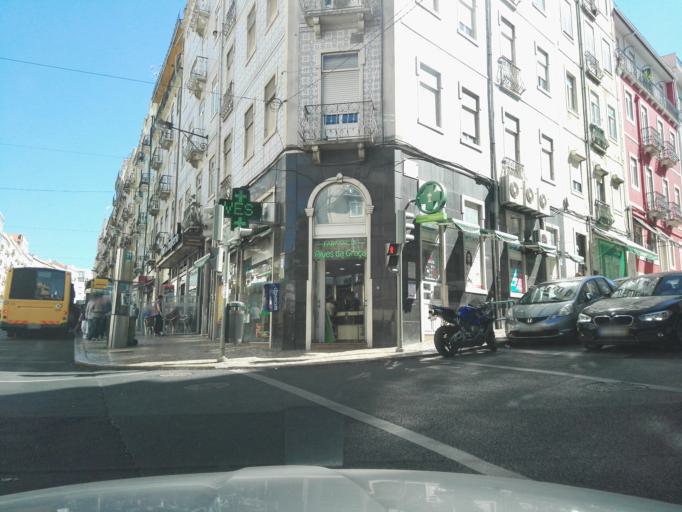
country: PT
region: Lisbon
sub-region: Lisbon
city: Lisbon
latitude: 38.7328
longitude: -9.1310
